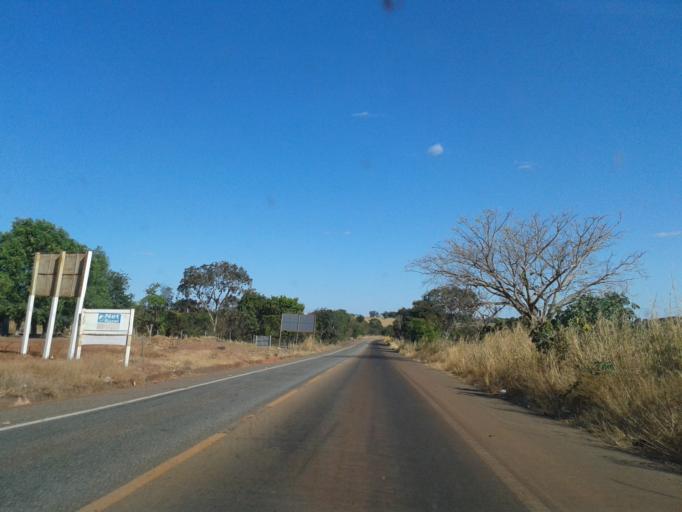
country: BR
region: Goias
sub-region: Mozarlandia
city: Mozarlandia
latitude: -14.7680
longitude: -50.5376
